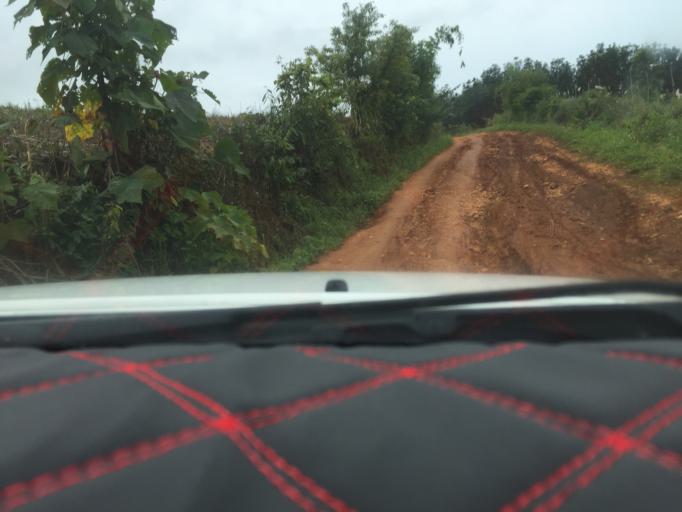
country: TH
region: Phayao
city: Phu Sang
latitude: 19.7678
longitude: 100.4975
